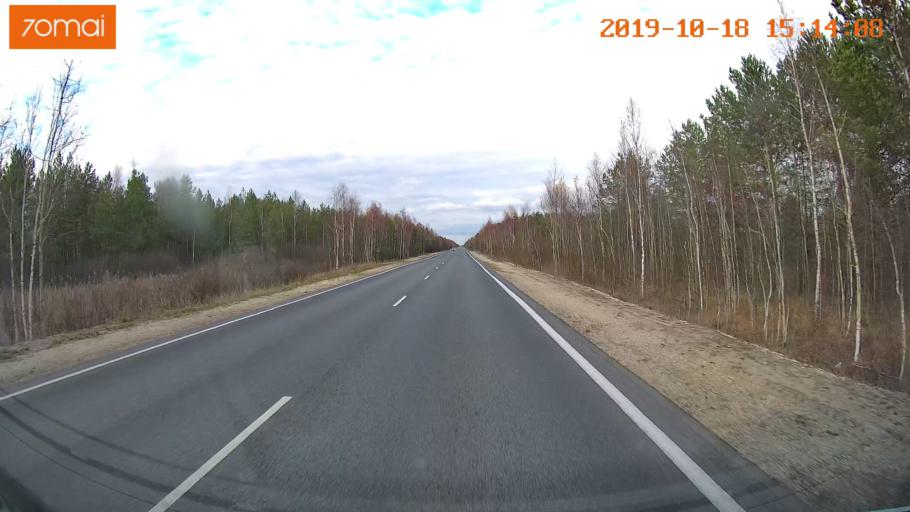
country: RU
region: Vladimir
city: Gus'-Khrustal'nyy
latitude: 55.5976
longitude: 40.7196
